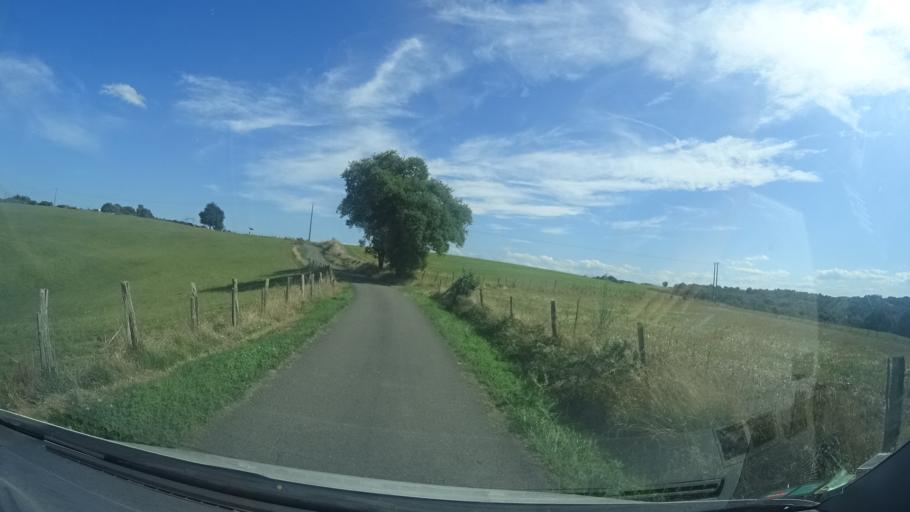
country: FR
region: Aquitaine
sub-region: Departement des Pyrenees-Atlantiques
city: Mont
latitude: 43.5061
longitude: -0.6851
